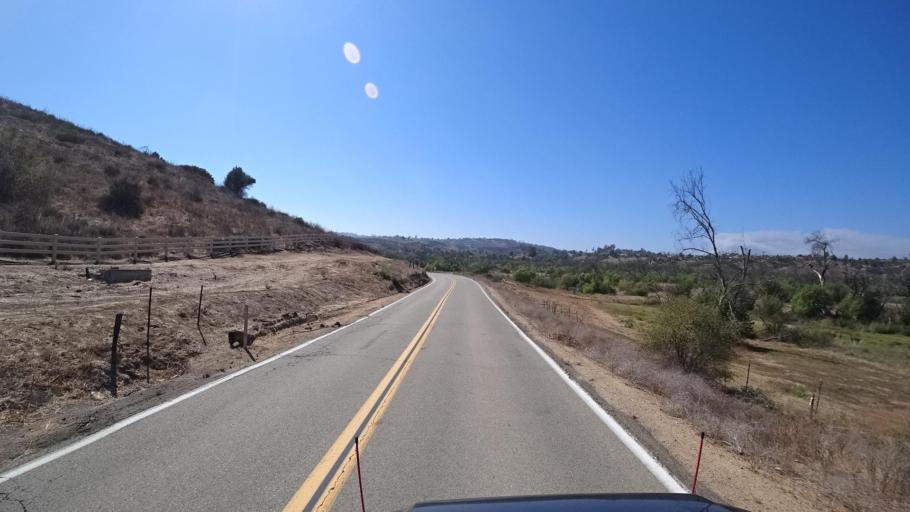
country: US
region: California
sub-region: San Diego County
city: Bonsall
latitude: 33.2983
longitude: -117.2096
